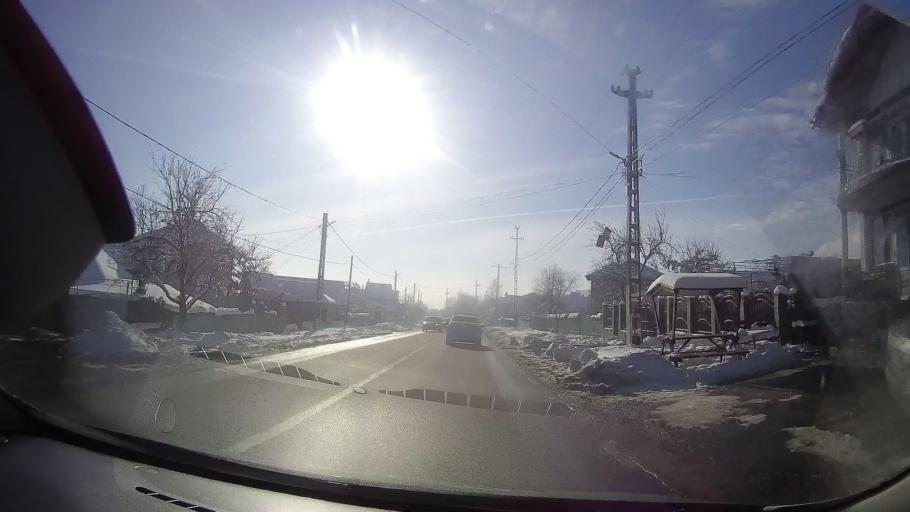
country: RO
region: Iasi
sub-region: Comuna Motca
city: Motca
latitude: 47.2487
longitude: 26.6084
